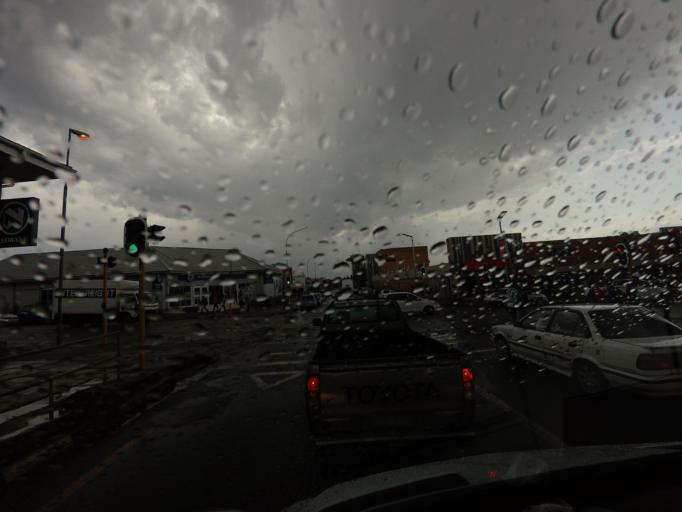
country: SZ
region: Manzini
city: Manzini
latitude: -26.4968
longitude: 31.3790
